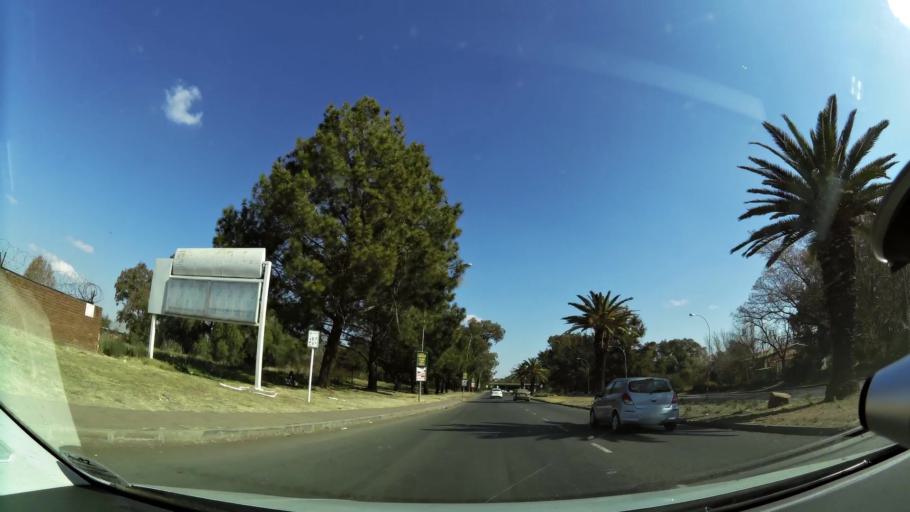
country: ZA
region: Orange Free State
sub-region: Mangaung Metropolitan Municipality
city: Bloemfontein
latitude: -29.1181
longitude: 26.2362
